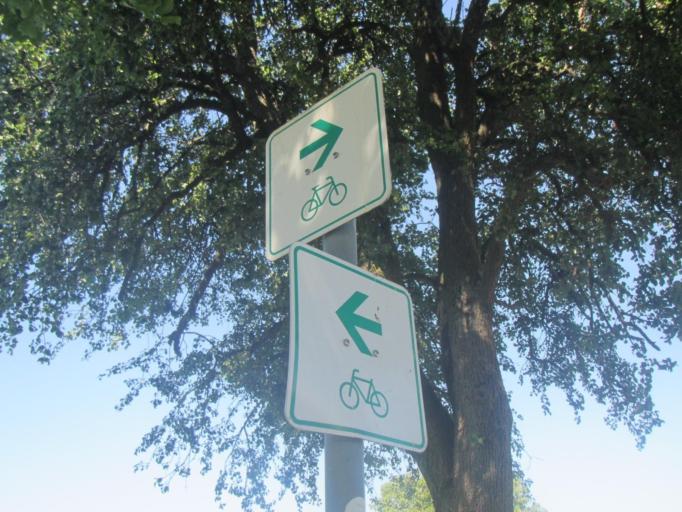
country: DE
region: Rheinland-Pfalz
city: Bad Bergzabern
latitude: 49.0760
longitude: 8.0010
